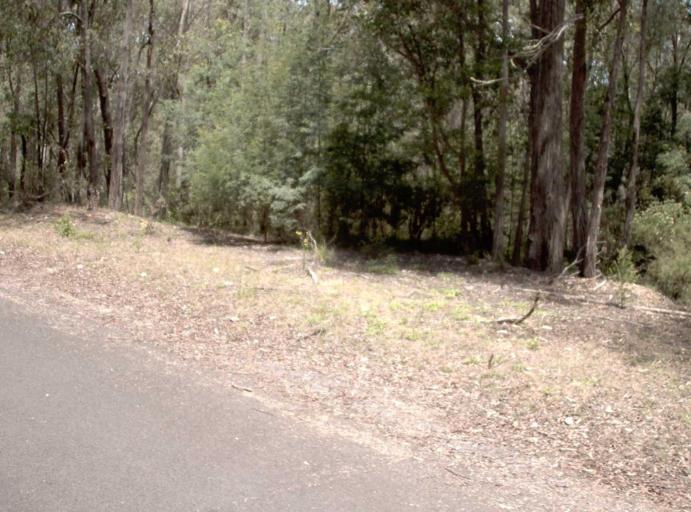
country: AU
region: New South Wales
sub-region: Bombala
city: Bombala
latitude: -37.4427
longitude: 148.9714
